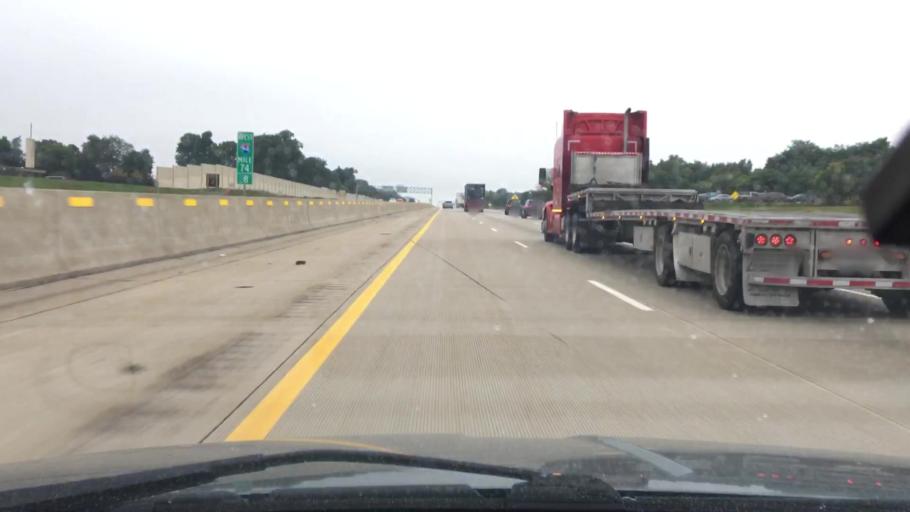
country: US
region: Michigan
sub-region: Kalamazoo County
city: Portage
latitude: 42.2379
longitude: -85.6152
